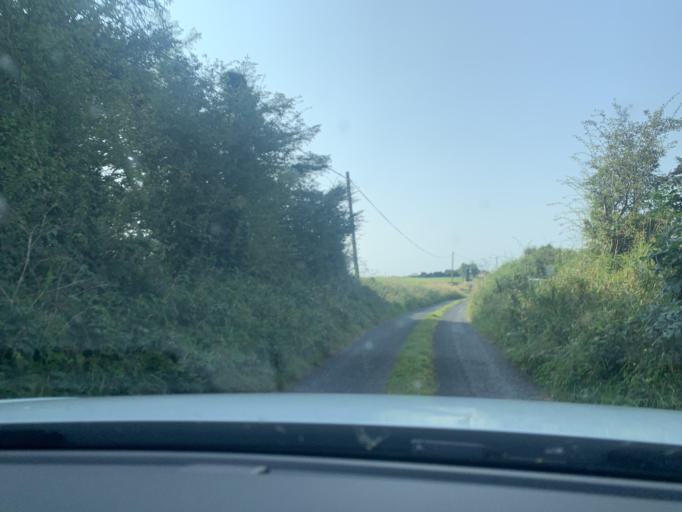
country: IE
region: Connaught
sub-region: Maigh Eo
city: Ballyhaunis
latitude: 53.7891
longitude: -8.7387
